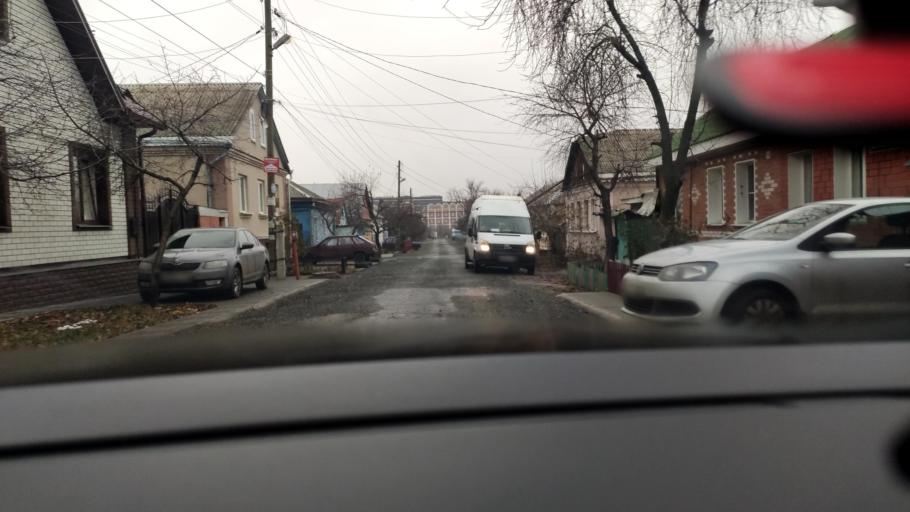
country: RU
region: Voronezj
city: Voronezh
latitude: 51.6275
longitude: 39.1708
